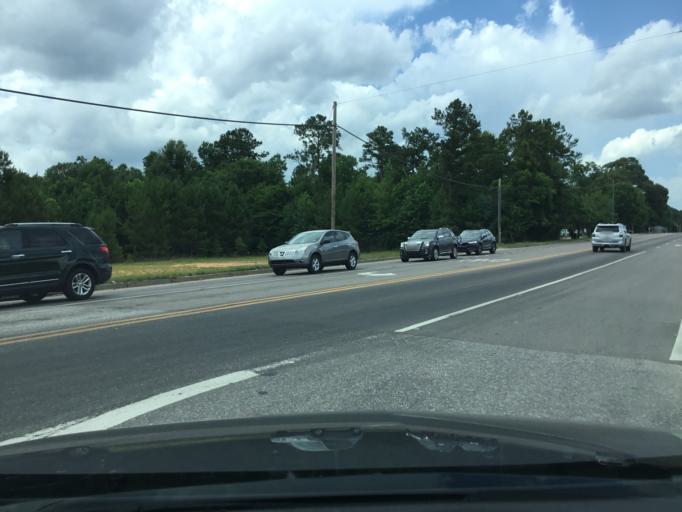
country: US
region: Alabama
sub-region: Montgomery County
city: Pike Road
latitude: 32.3470
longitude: -86.0949
